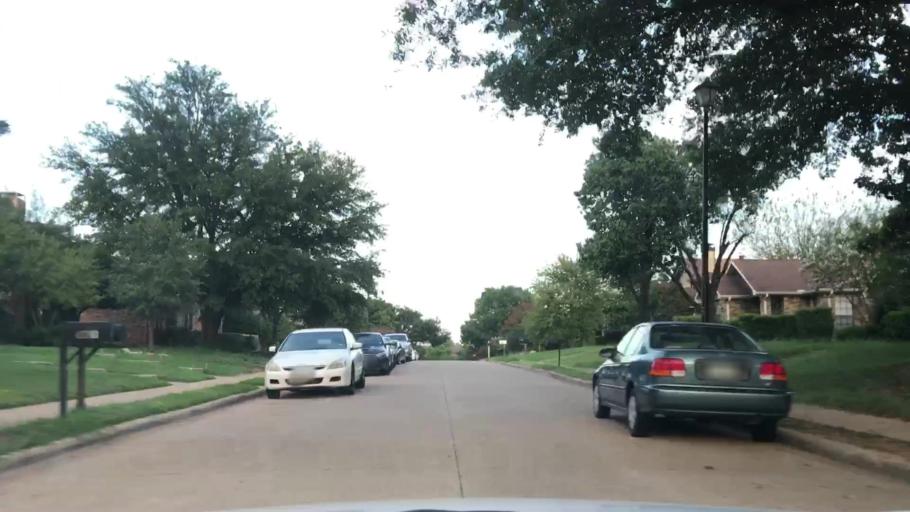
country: US
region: Texas
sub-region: Dallas County
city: Addison
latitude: 33.0048
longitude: -96.8602
